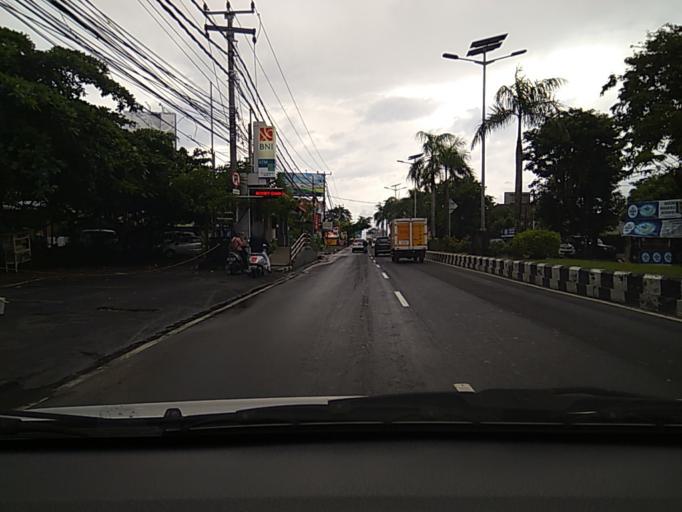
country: ID
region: Bali
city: Bualu
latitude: -8.7929
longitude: 115.2150
